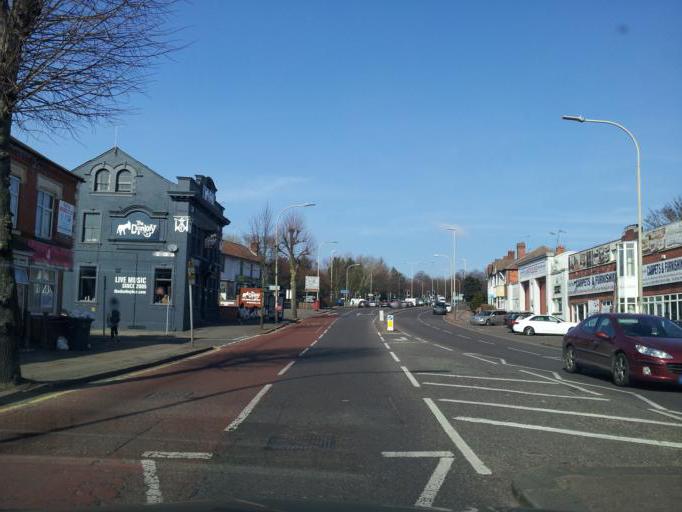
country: GB
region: England
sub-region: City of Leicester
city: Leicester
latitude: 52.6161
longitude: -1.1258
